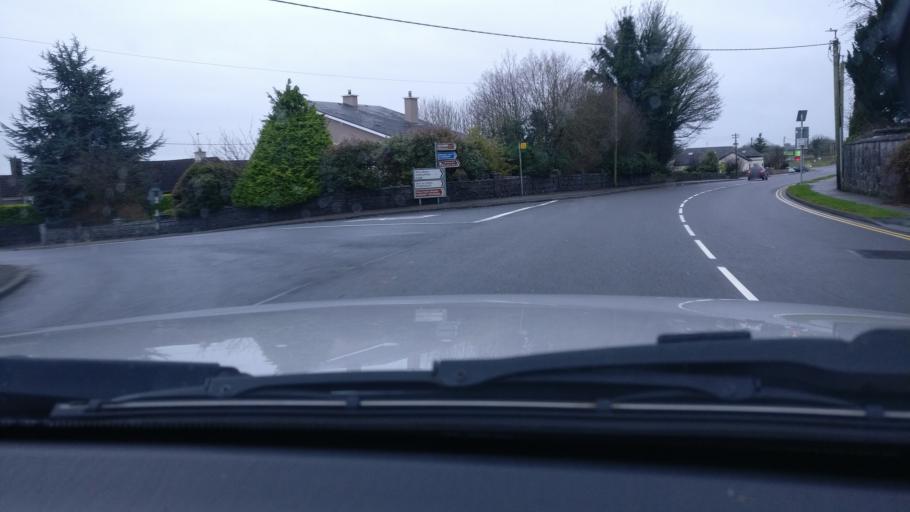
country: IE
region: Connaught
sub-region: County Galway
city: Ballinasloe
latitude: 53.3210
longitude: -8.2416
